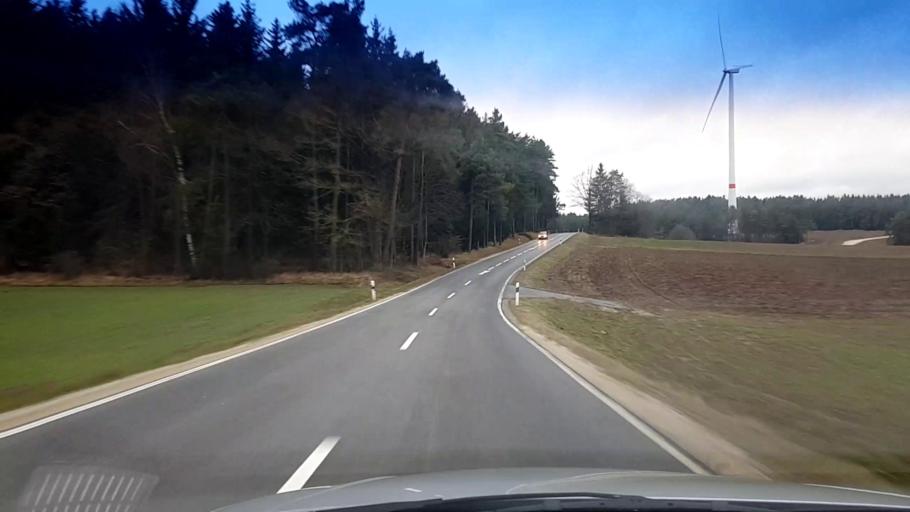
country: DE
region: Bavaria
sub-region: Upper Franconia
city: Wattendorf
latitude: 50.0125
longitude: 11.1312
